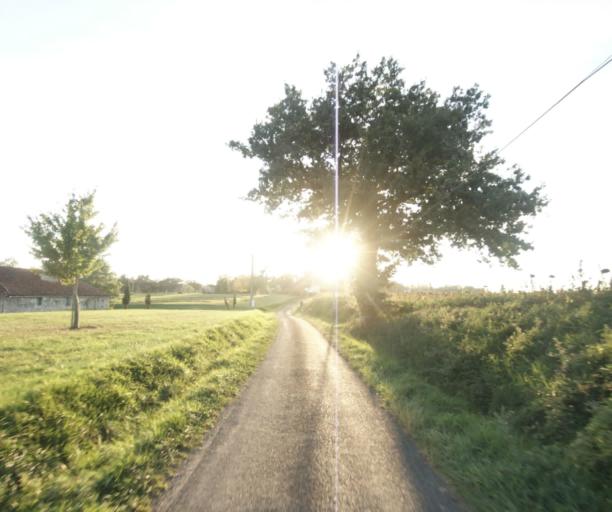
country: FR
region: Midi-Pyrenees
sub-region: Departement du Gers
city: Gondrin
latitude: 43.8551
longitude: 0.2589
